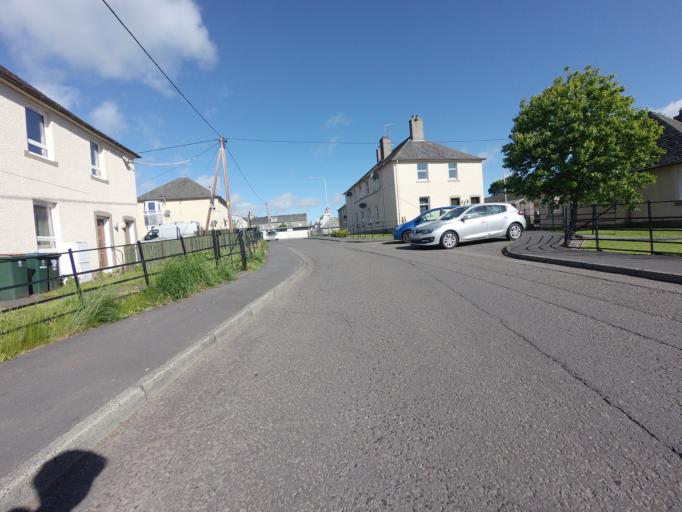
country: GB
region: Scotland
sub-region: Perth and Kinross
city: Auchterarder
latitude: 56.2939
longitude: -3.7098
